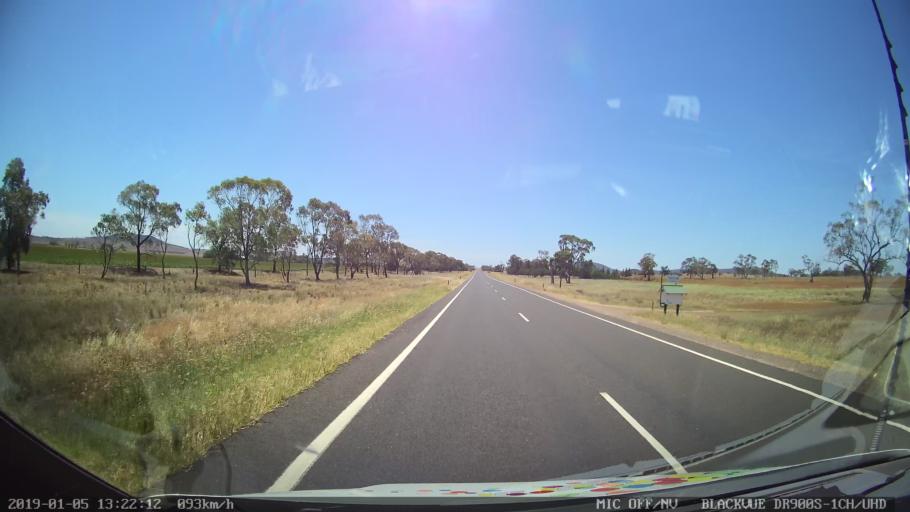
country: AU
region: New South Wales
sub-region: Gunnedah
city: Gunnedah
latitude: -31.0882
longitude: 149.9586
